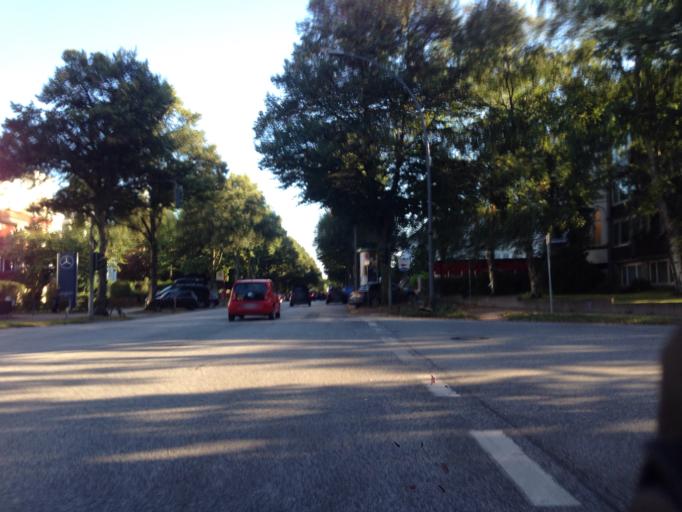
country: DE
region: Hamburg
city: Eimsbuettel
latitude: 53.5778
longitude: 9.9890
